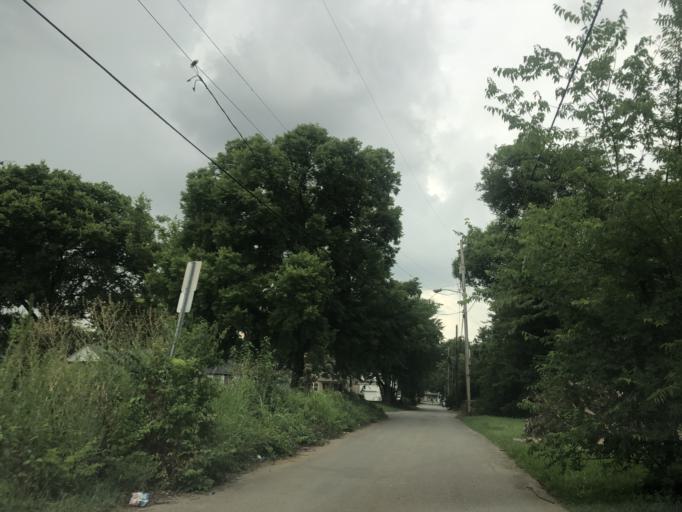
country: US
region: Tennessee
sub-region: Davidson County
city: Nashville
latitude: 36.1725
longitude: -86.8035
